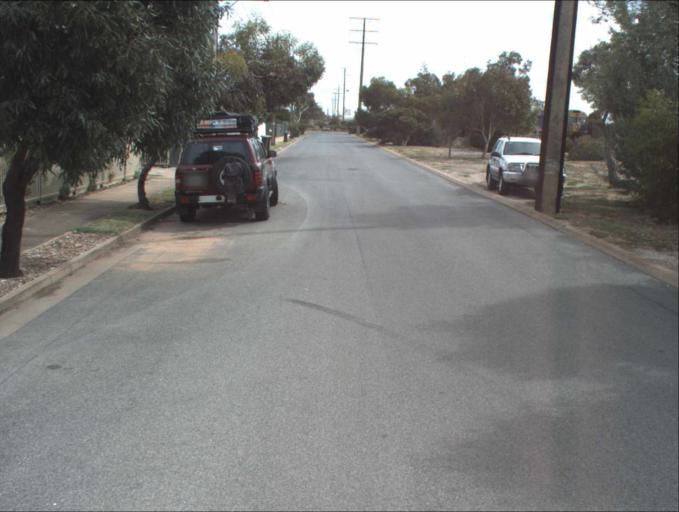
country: AU
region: South Australia
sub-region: Port Adelaide Enfield
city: Birkenhead
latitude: -34.8159
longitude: 138.5074
